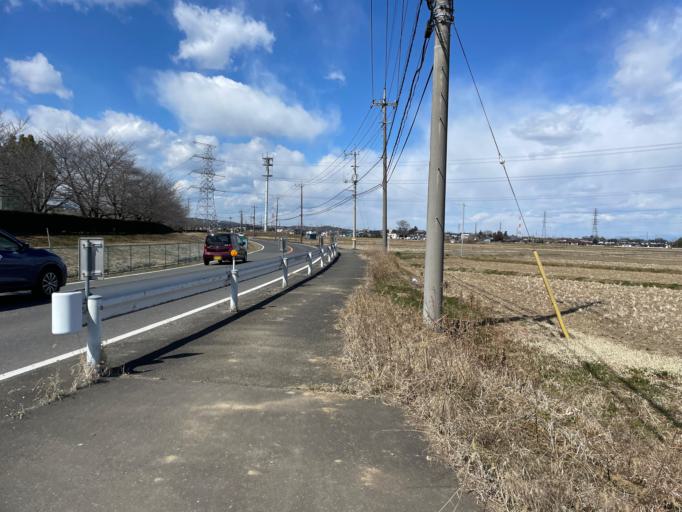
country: JP
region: Saitama
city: Sakado
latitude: 35.9810
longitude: 139.4152
